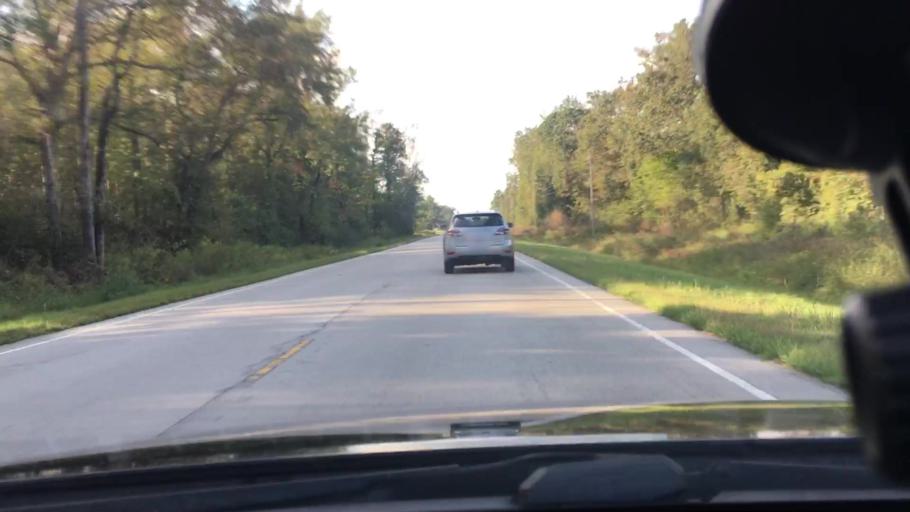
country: US
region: North Carolina
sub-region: Pitt County
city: Windsor
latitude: 35.4894
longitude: -77.3054
